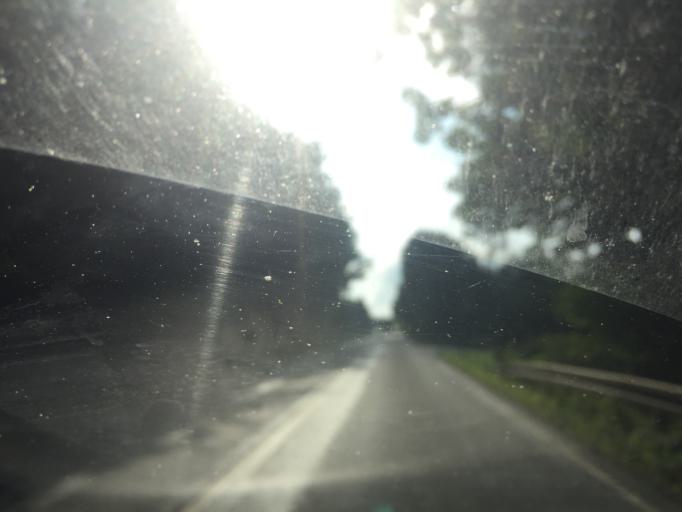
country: DK
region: Zealand
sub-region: Lejre Kommune
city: Ejby
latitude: 55.6506
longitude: 11.8097
